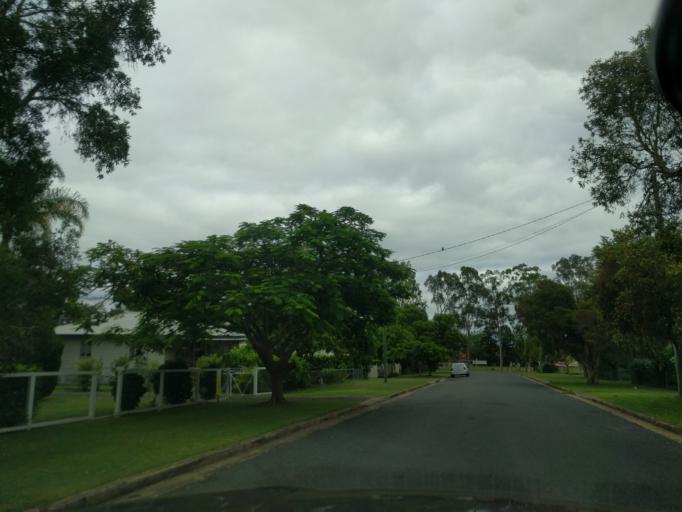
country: AU
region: Queensland
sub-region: Logan
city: Cedar Vale
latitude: -27.9894
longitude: 153.0056
